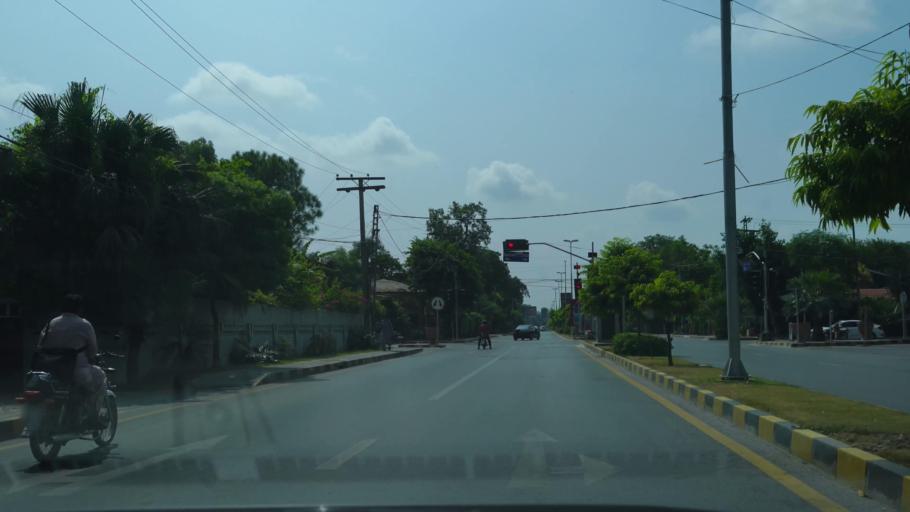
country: PK
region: Punjab
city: Lahore
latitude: 31.5220
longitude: 74.3712
